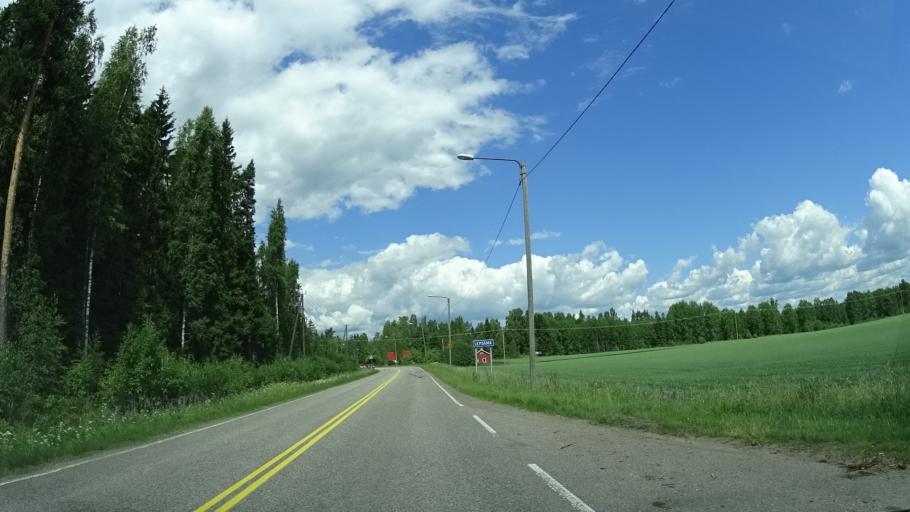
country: FI
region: Uusimaa
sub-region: Helsinki
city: Espoo
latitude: 60.3718
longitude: 24.6410
